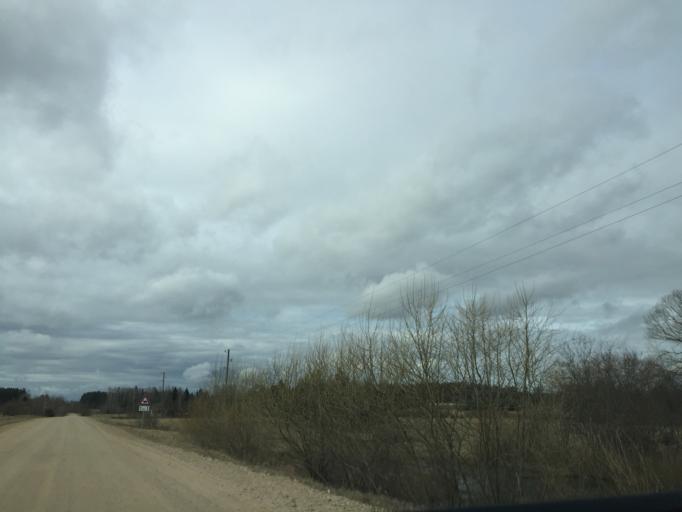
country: LV
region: Daugavpils
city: Daugavpils
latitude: 55.9521
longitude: 26.7006
